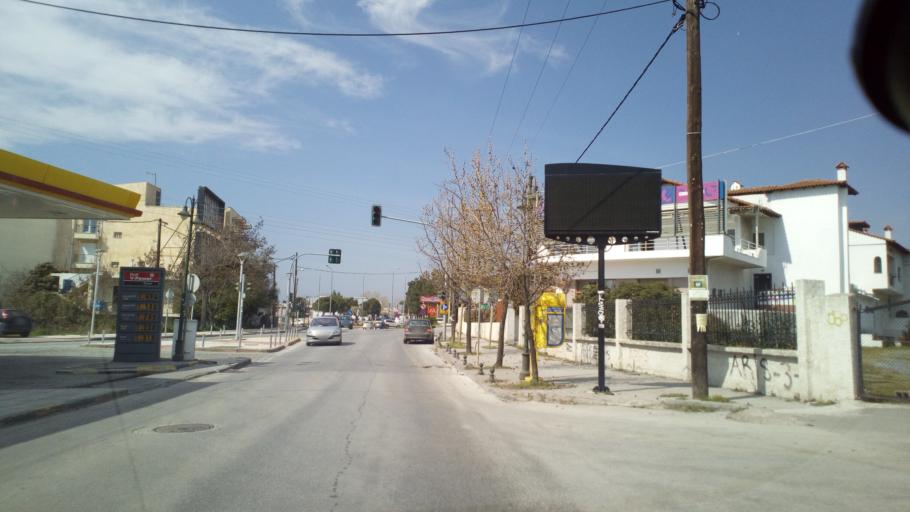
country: GR
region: Central Macedonia
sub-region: Nomos Thessalonikis
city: Thermi
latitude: 40.5518
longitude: 23.0192
